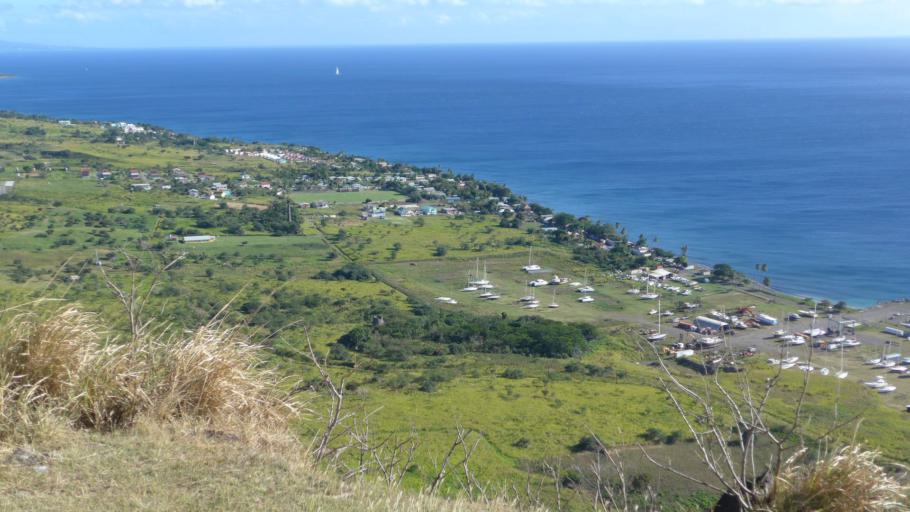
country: KN
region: Saint Anne Sandy Point
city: Sandy Point Town
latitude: 17.3460
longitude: -62.8356
